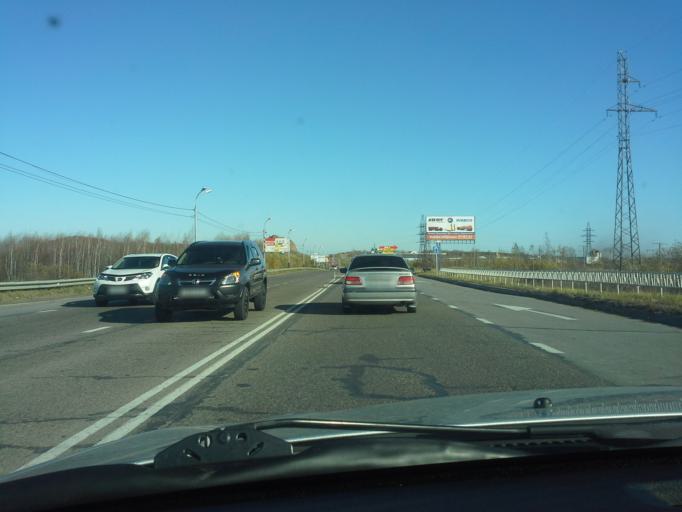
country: RU
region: Khabarovsk Krai
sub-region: Khabarovskiy Rayon
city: Khabarovsk
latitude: 48.5479
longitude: 135.0567
